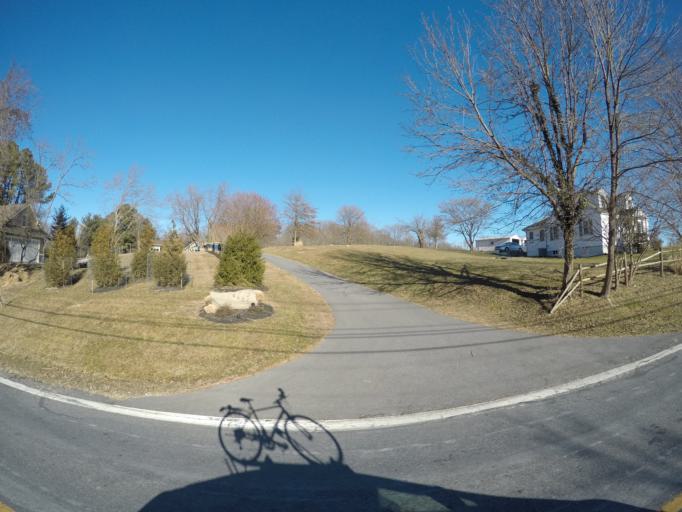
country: US
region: Maryland
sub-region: Howard County
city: Ilchester
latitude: 39.2499
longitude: -76.7773
